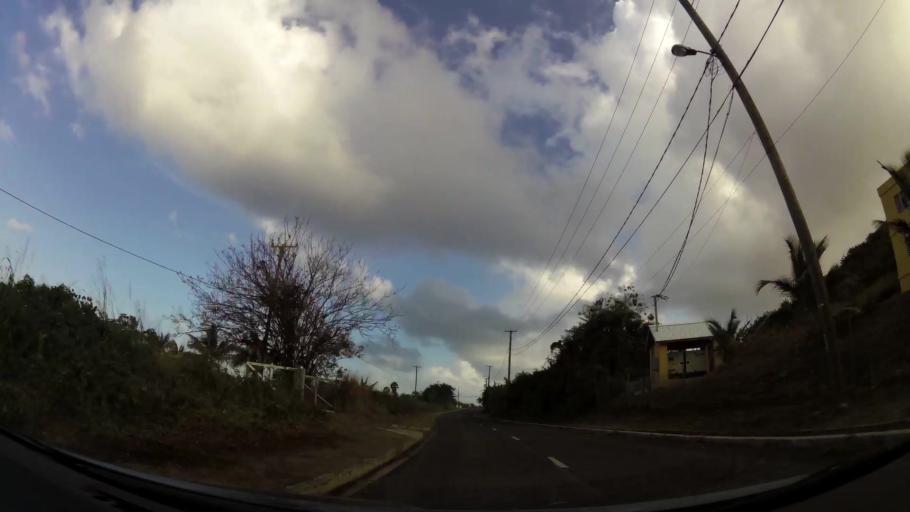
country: KN
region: Saint James Windwa
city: Newcastle
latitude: 17.1913
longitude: -62.5648
